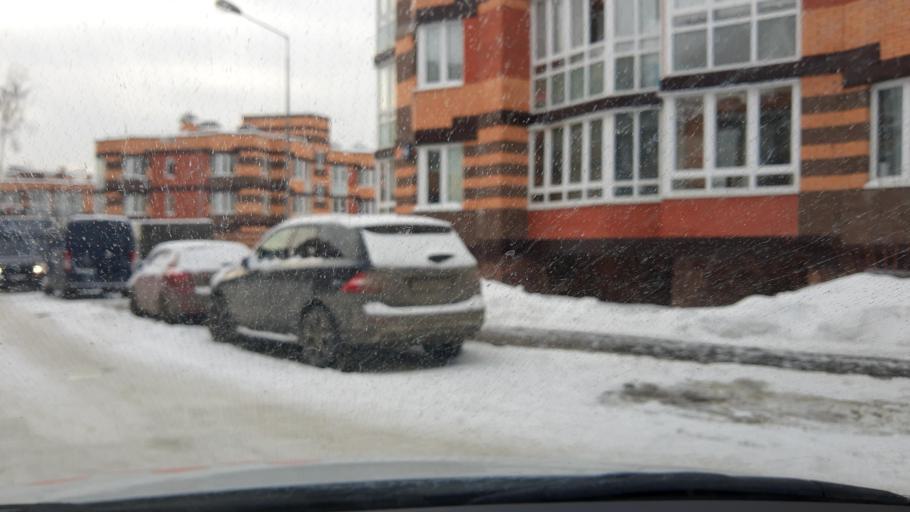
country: RU
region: Moskovskaya
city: Kommunarka
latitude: 55.5501
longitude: 37.4998
